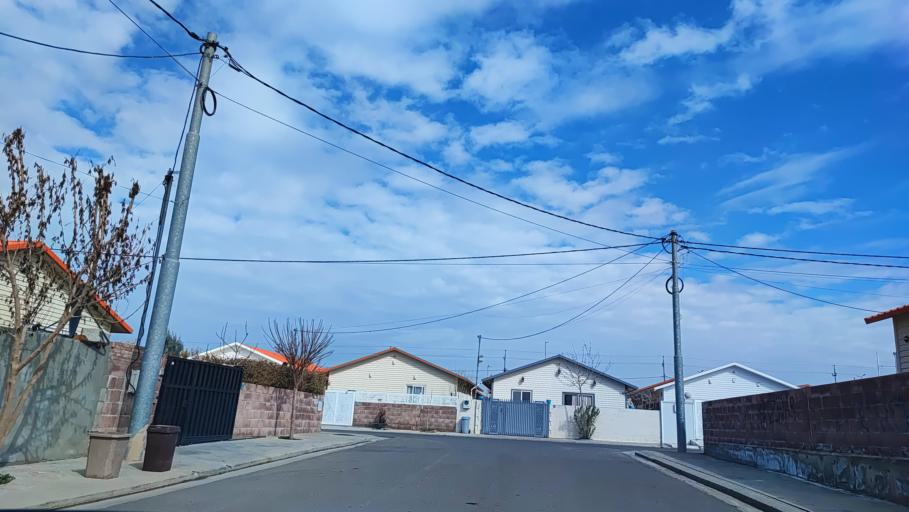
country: IQ
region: Arbil
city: Erbil
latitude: 36.2848
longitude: 44.0689
